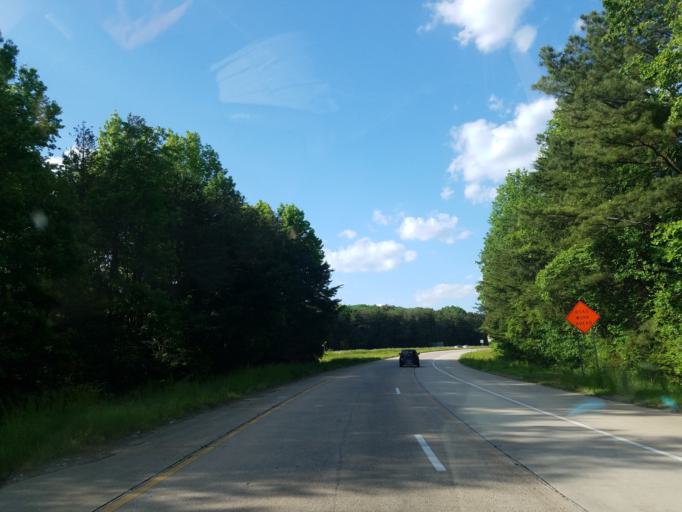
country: US
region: Georgia
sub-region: Forsyth County
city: Cumming
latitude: 34.2109
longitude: -84.1213
